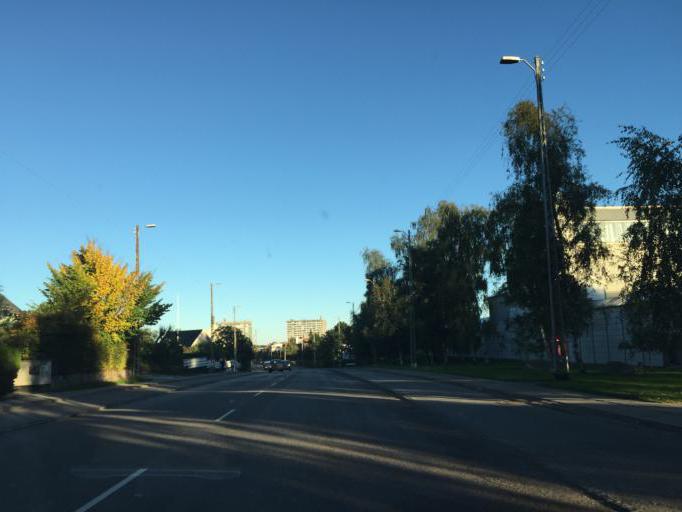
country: DK
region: Capital Region
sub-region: Herlev Kommune
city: Herlev
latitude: 55.7623
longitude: 12.4435
